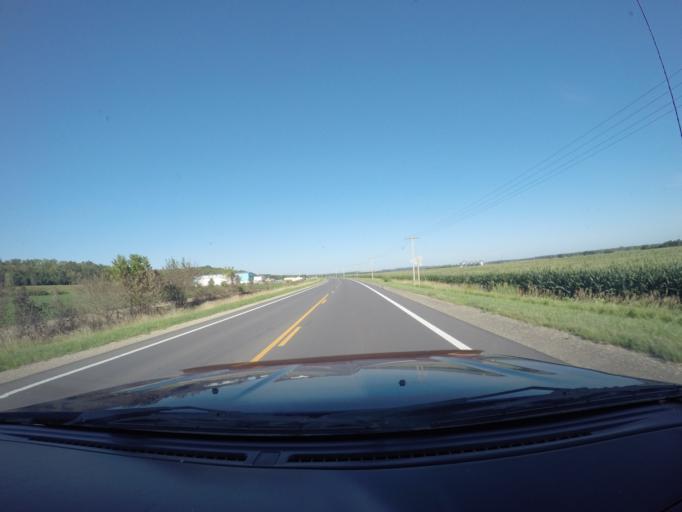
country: US
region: Kansas
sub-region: Douglas County
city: Lawrence
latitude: 39.0657
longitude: -95.3302
